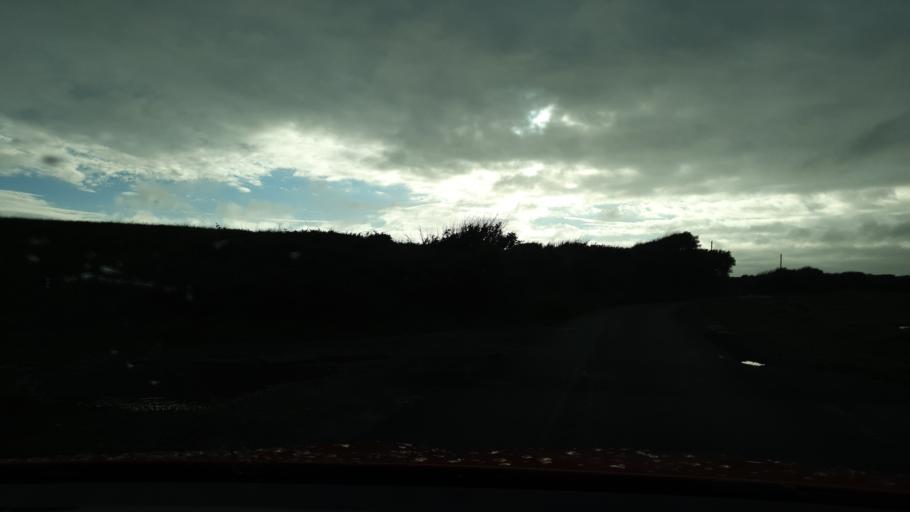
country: GB
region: England
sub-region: Cumbria
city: Barrow in Furness
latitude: 54.0655
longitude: -3.2217
